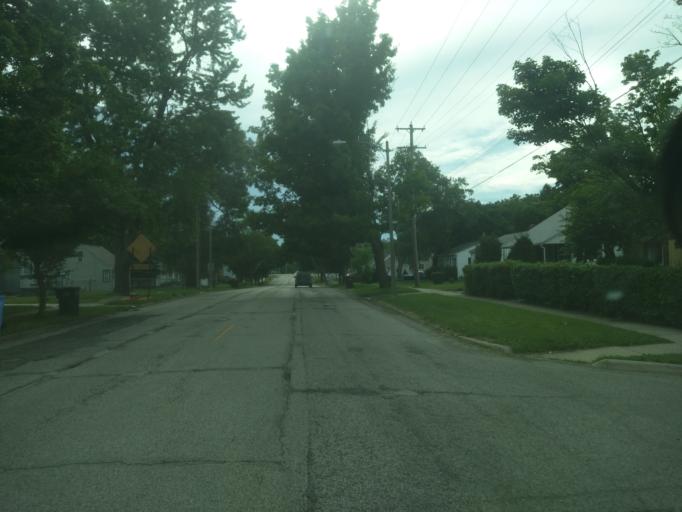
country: US
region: Michigan
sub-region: Ingham County
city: Lansing
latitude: 42.6902
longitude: -84.5452
